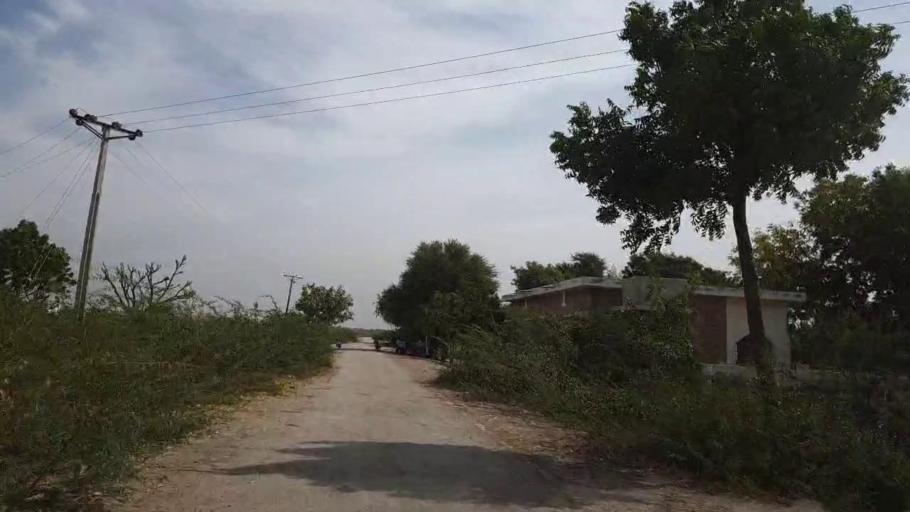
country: PK
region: Sindh
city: Kunri
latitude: 25.2077
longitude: 69.5859
